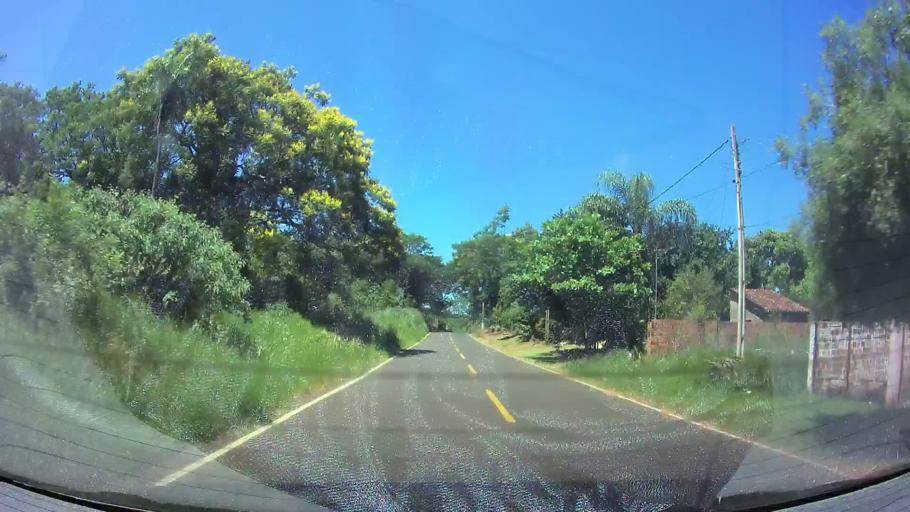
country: PY
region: Central
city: Aregua
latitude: -25.2537
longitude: -57.4441
